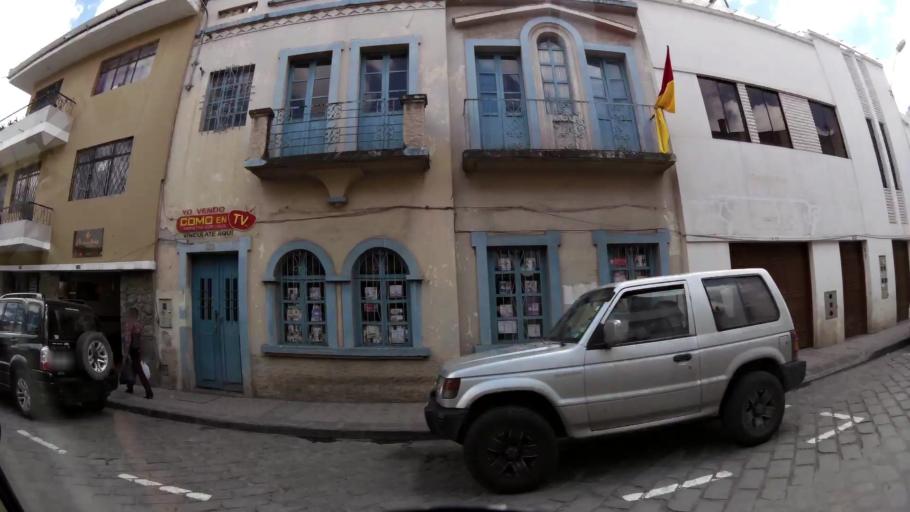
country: EC
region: Azuay
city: Cuenca
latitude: -2.8994
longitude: -78.9984
